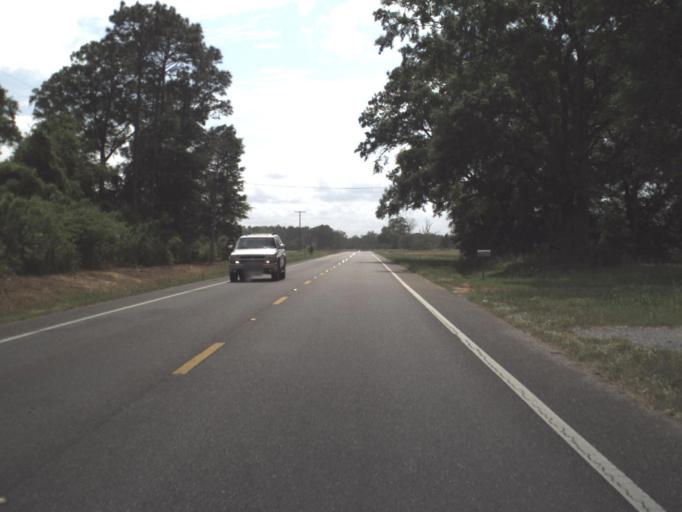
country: US
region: Alabama
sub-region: Escambia County
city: East Brewton
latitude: 30.9788
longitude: -87.1221
